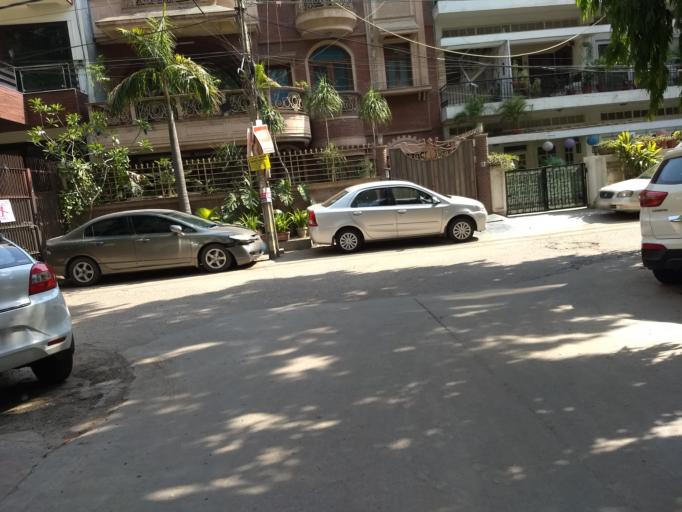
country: IN
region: NCT
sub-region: New Delhi
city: New Delhi
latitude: 28.5661
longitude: 77.1973
